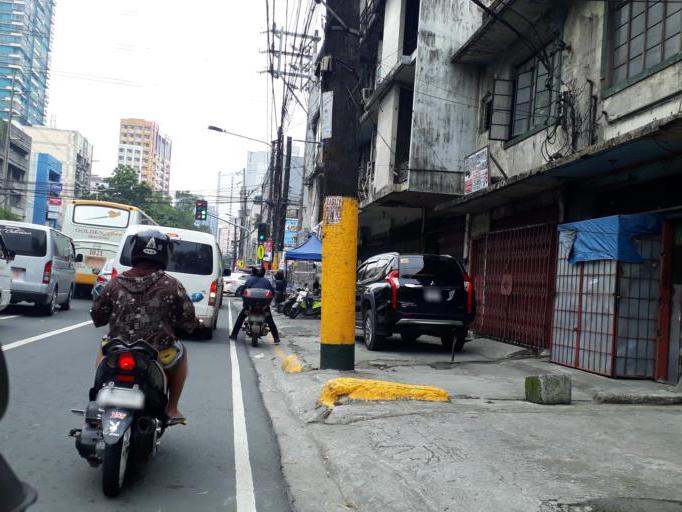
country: PH
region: Metro Manila
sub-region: City of Manila
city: Manila
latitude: 14.6108
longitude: 120.9760
